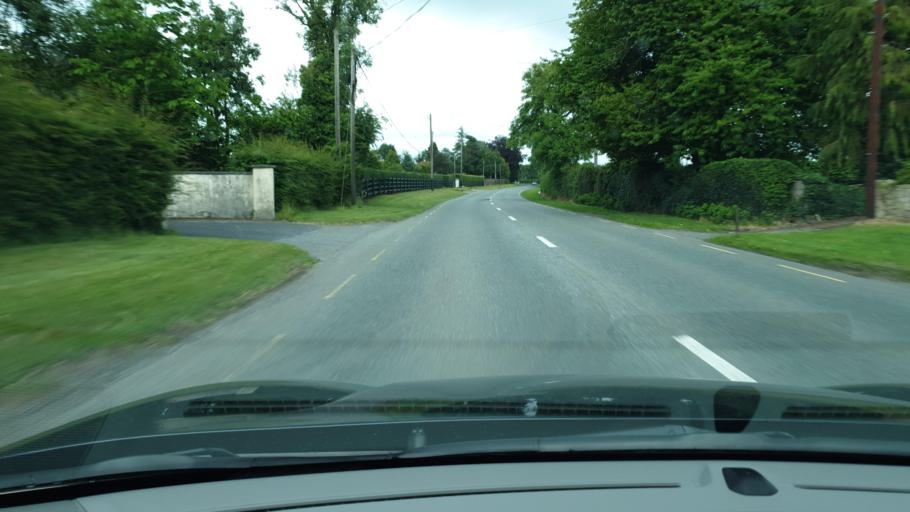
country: IE
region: Leinster
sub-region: An Mhi
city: Dunboyne
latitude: 53.4535
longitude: -6.4922
